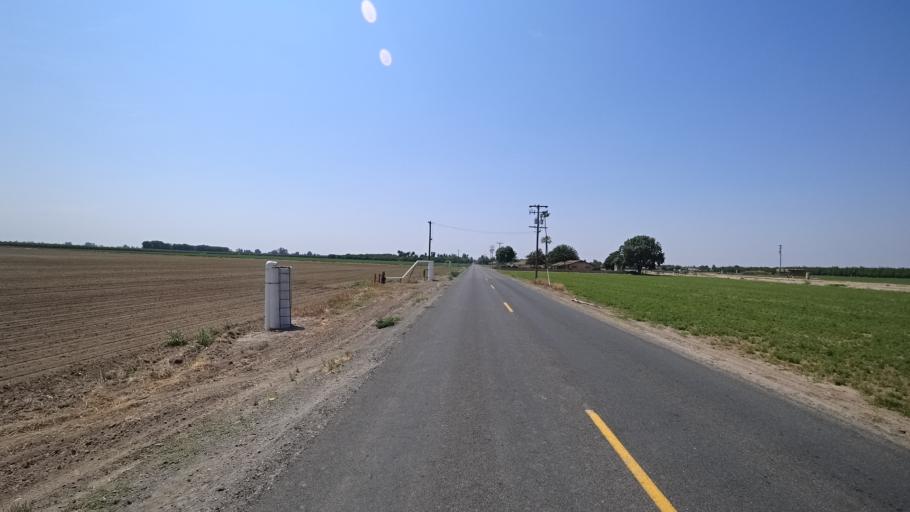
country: US
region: California
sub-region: Kings County
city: Lemoore
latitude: 36.3259
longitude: -119.7628
